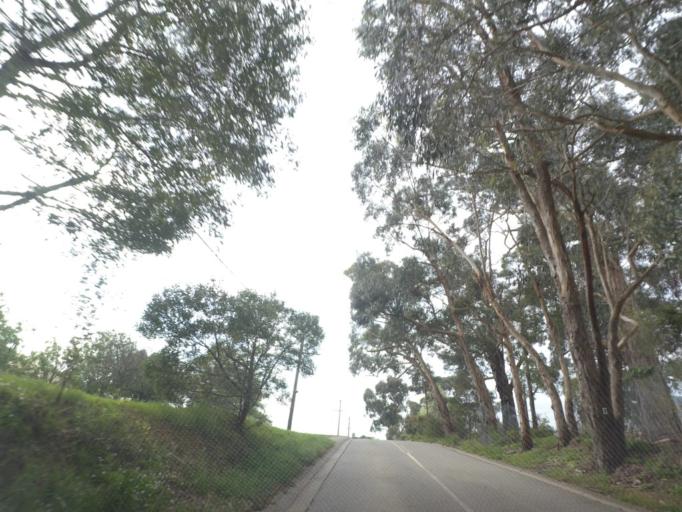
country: AU
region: Victoria
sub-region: Knox
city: The Basin
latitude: -37.8536
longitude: 145.3231
